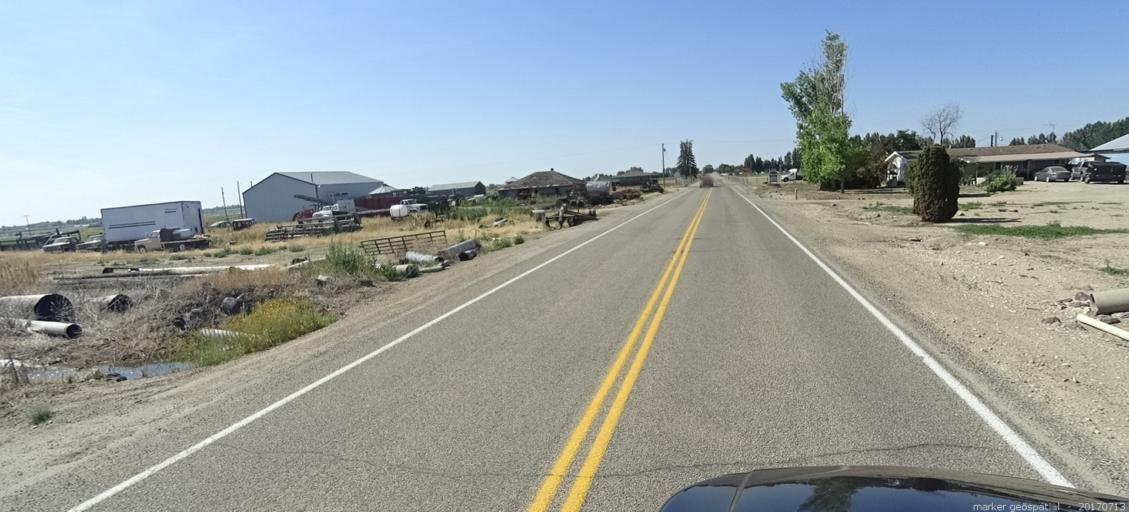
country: US
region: Idaho
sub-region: Ada County
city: Kuna
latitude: 43.5184
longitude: -116.3743
